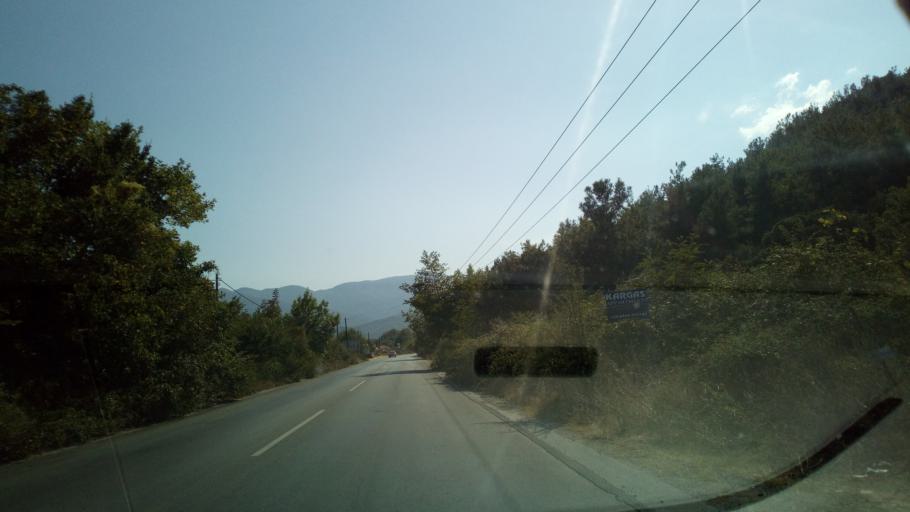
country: GR
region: Central Macedonia
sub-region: Nomos Thessalonikis
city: Stavros
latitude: 40.6087
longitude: 23.7771
